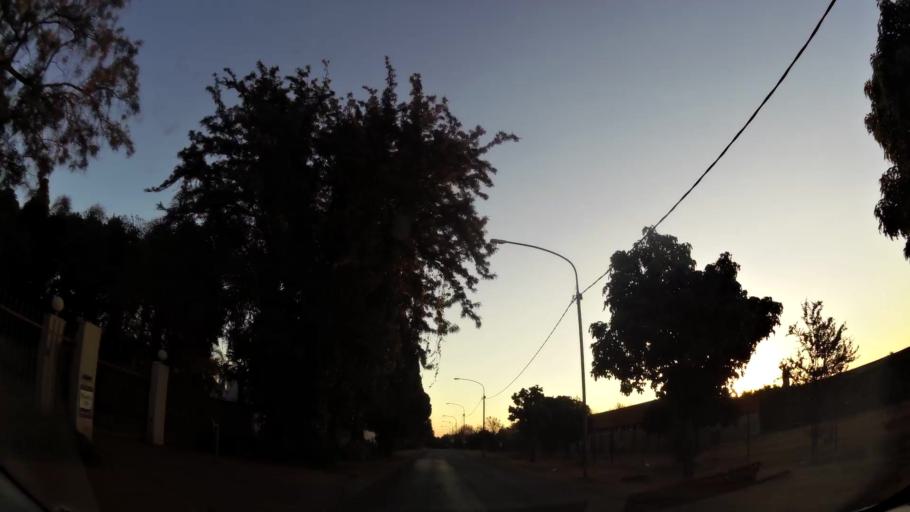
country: ZA
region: Gauteng
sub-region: City of Tshwane Metropolitan Municipality
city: Centurion
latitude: -25.8489
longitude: 28.1552
